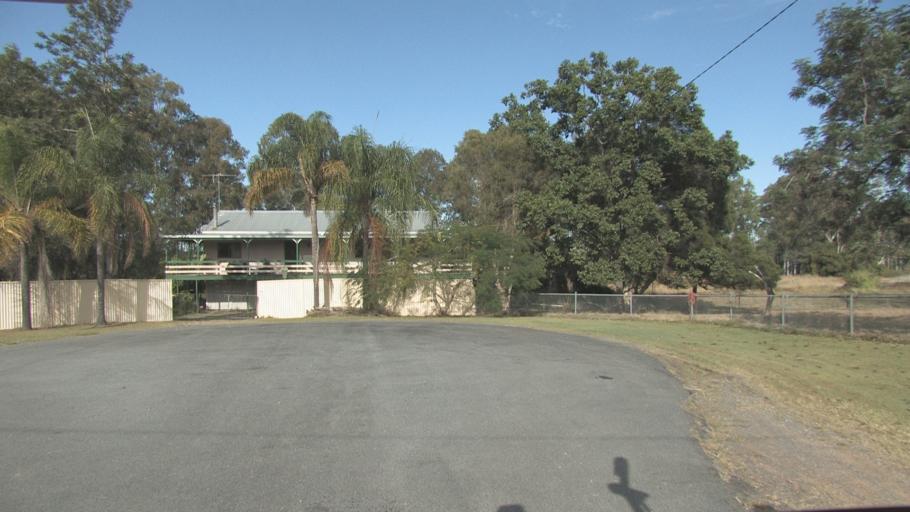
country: AU
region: Queensland
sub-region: Logan
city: Chambers Flat
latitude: -27.7507
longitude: 153.0599
